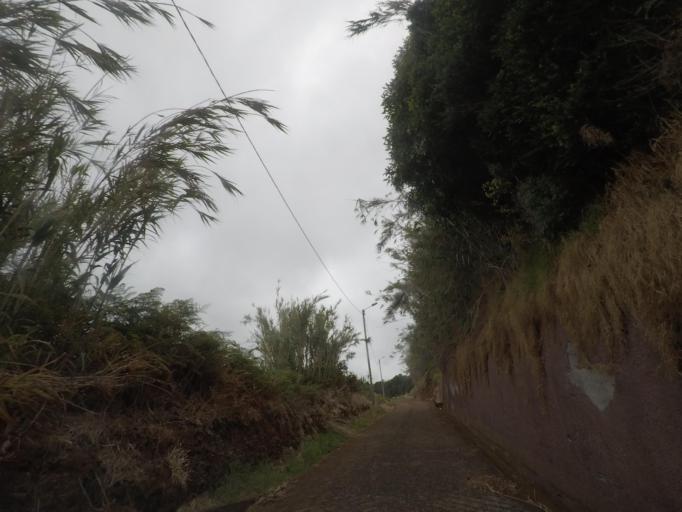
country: PT
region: Madeira
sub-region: Porto Moniz
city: Porto Moniz
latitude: 32.8630
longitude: -17.1803
